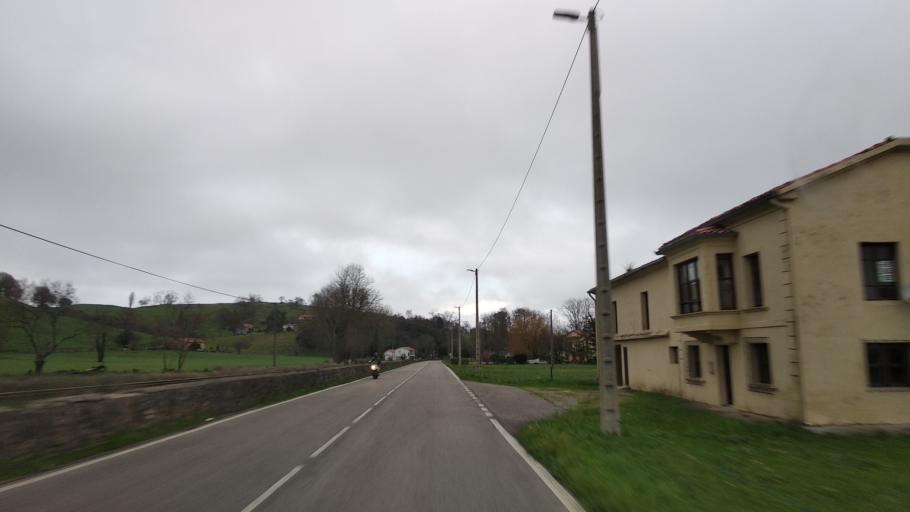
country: ES
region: Cantabria
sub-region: Provincia de Cantabria
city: Entrambasaguas
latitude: 43.4011
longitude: -3.7278
